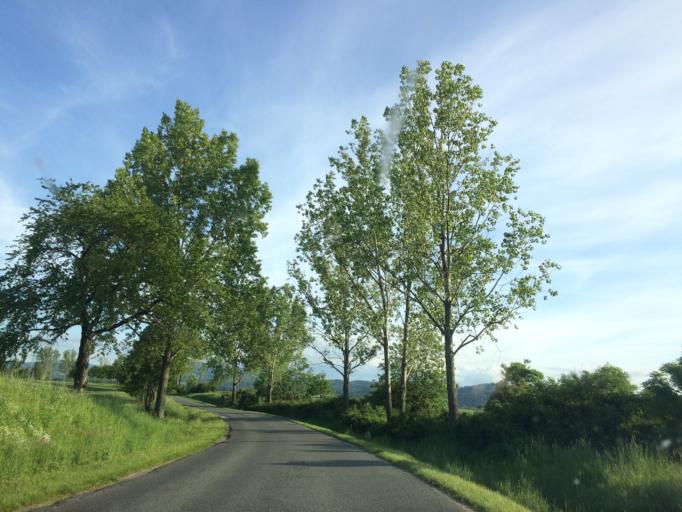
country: PL
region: Lower Silesian Voivodeship
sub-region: Powiat swidnicki
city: Swidnica
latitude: 50.8098
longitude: 16.4923
